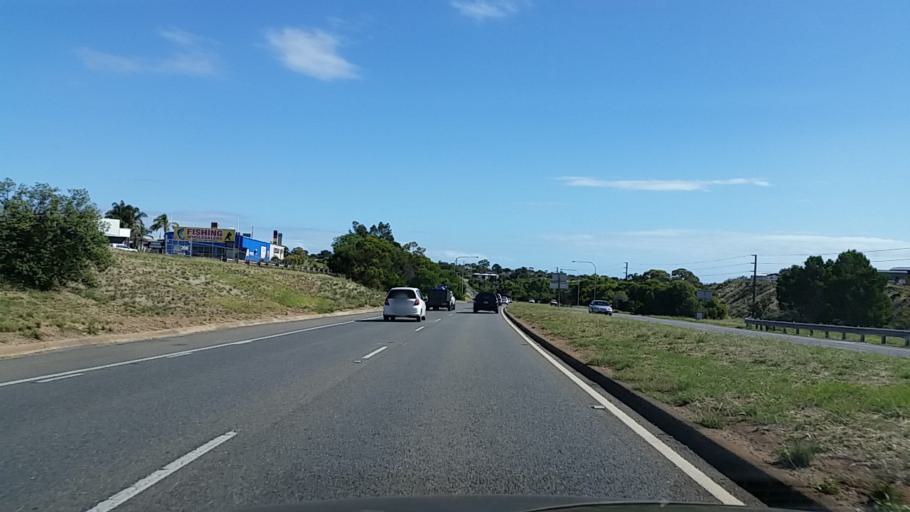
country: AU
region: South Australia
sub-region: Onkaparinga
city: Morphett Vale
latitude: -35.1189
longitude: 138.4898
